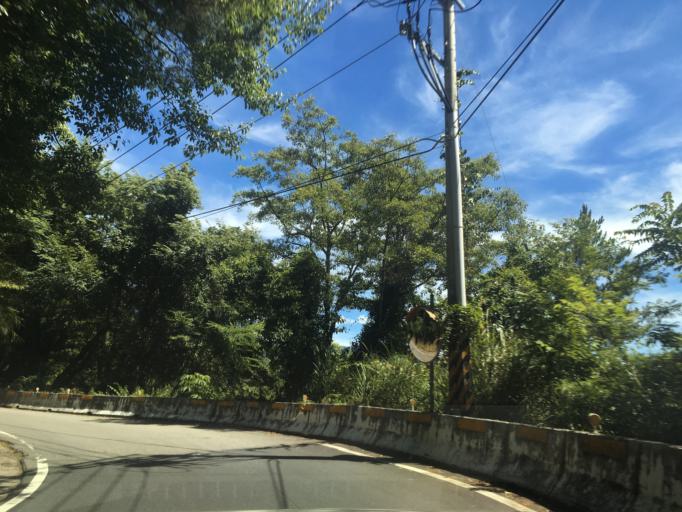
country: TW
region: Taiwan
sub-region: Nantou
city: Puli
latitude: 24.2227
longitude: 121.2594
